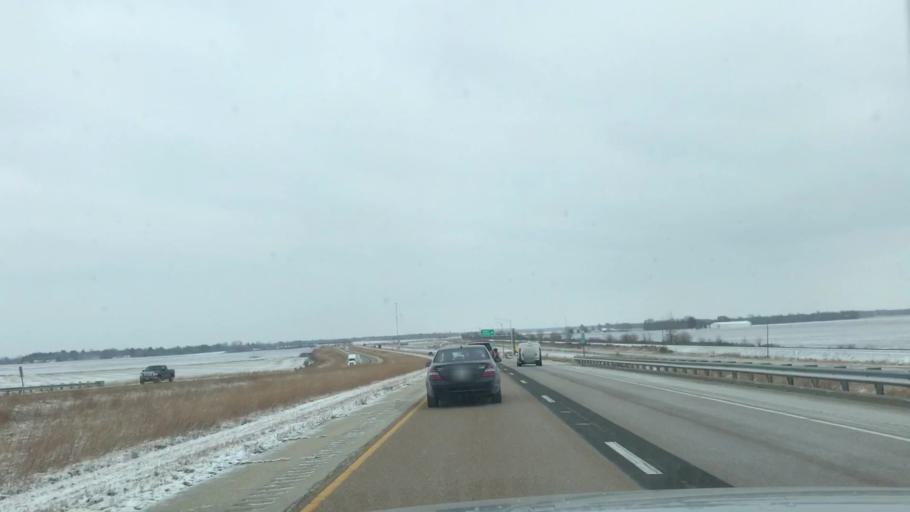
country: US
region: Illinois
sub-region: Montgomery County
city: Litchfield
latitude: 39.2188
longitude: -89.6490
